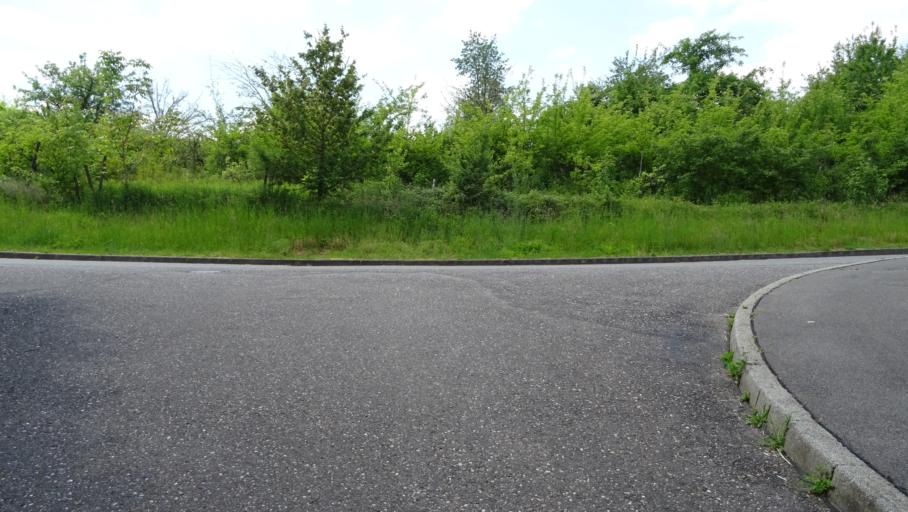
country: DE
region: Baden-Wuerttemberg
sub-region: Karlsruhe Region
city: Obrigheim
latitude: 49.3493
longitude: 9.0899
